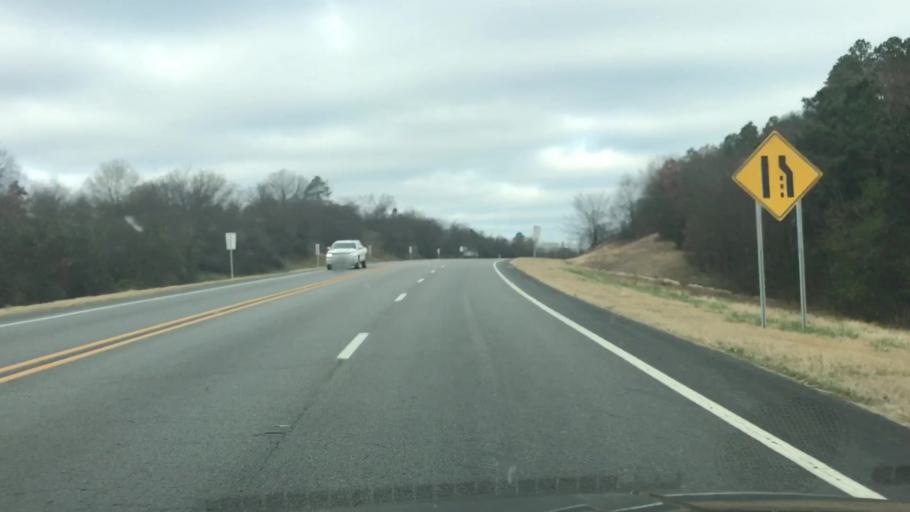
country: US
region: Arkansas
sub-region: Scott County
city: Waldron
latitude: 34.8829
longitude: -94.1050
